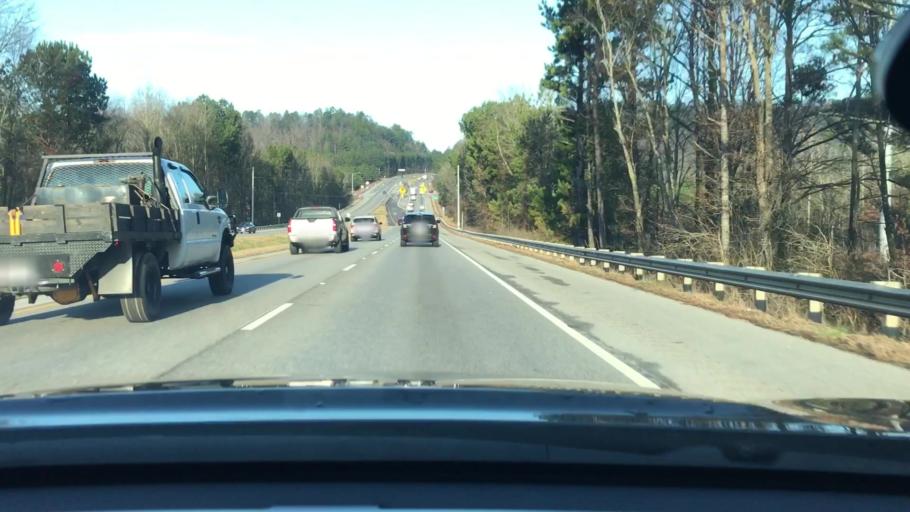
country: US
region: Alabama
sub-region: Shelby County
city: Chelsea
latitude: 33.3534
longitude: -86.6473
